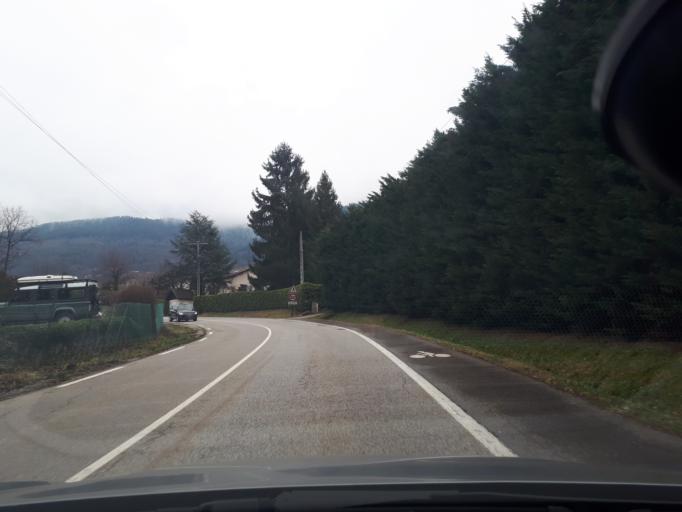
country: FR
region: Rhone-Alpes
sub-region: Departement de l'Isere
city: Vaulnaveys-le-Haut
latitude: 45.1292
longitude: 5.8235
